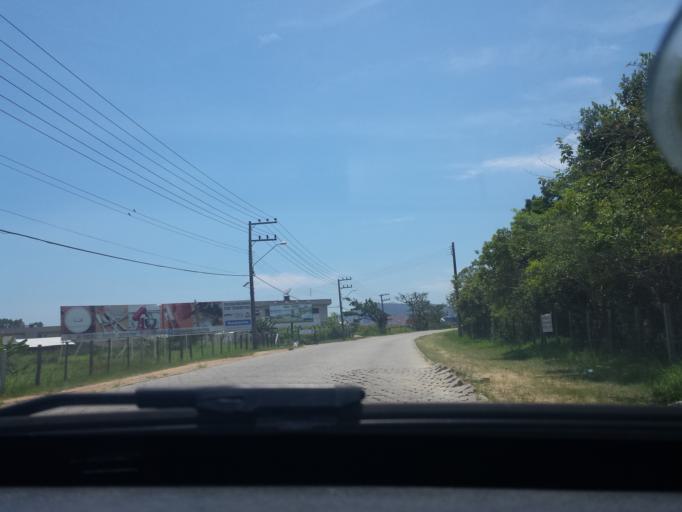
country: BR
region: Santa Catarina
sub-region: Porto Belo
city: Porto Belo
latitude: -27.1569
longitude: -48.5899
